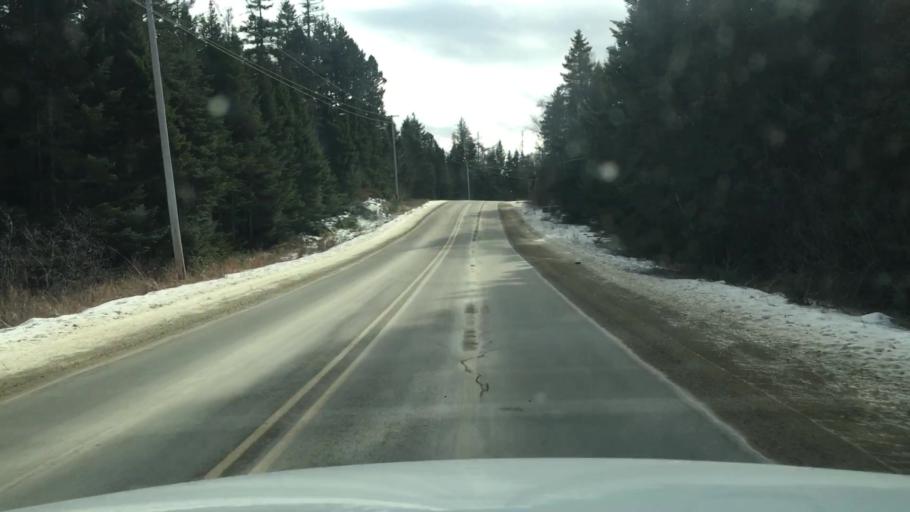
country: US
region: Maine
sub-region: Washington County
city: Jonesport
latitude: 44.6348
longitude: -67.5935
